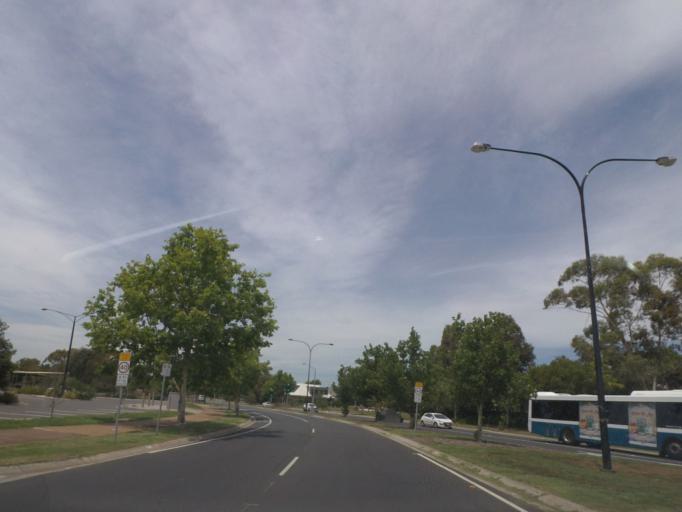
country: AU
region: Victoria
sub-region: Melton
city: Caroline Springs
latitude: -37.7466
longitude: 144.7358
